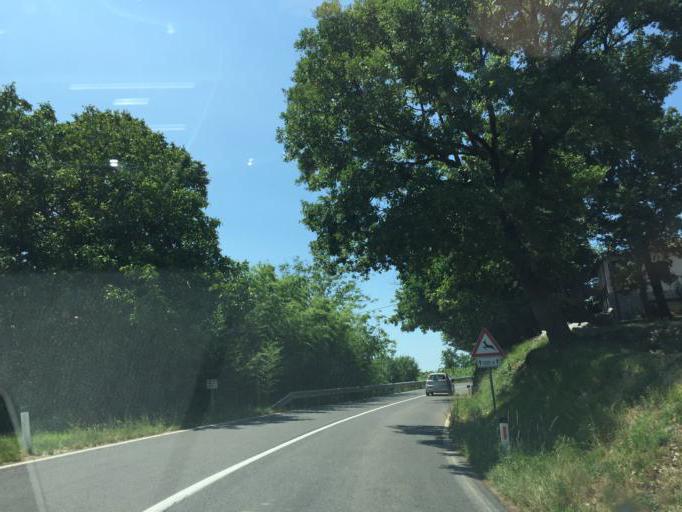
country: IT
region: Friuli Venezia Giulia
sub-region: Provincia di Trieste
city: Zolla
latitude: 45.7552
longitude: 13.8450
